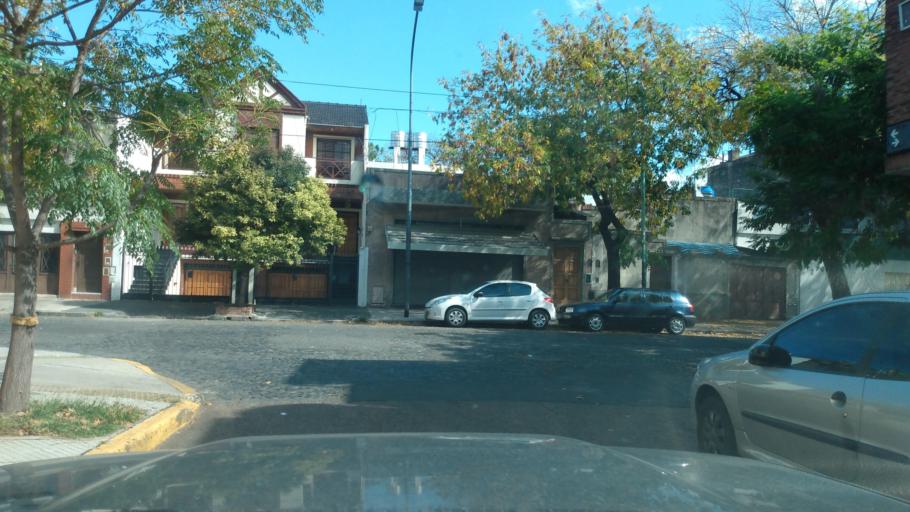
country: AR
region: Buenos Aires
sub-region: Partido de General San Martin
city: General San Martin
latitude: -34.5654
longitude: -58.4984
